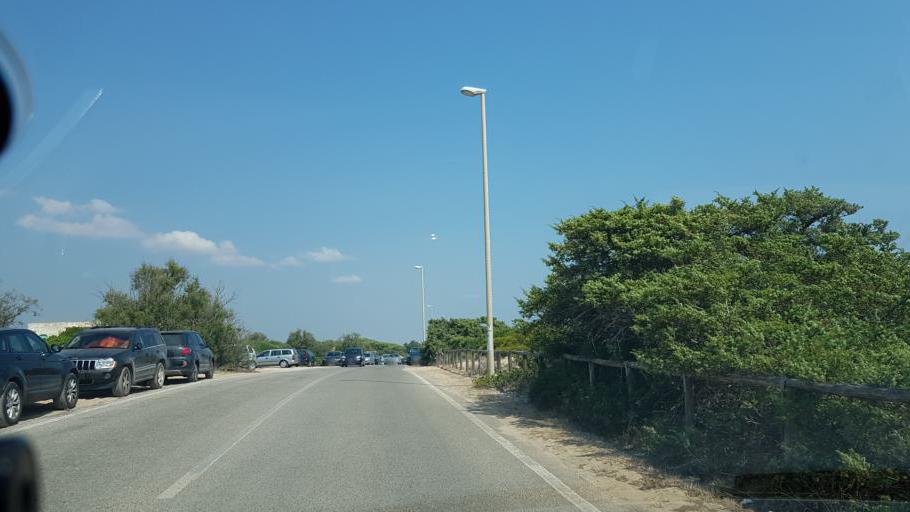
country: IT
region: Apulia
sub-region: Provincia di Taranto
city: Maruggio
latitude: 40.3010
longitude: 17.6054
